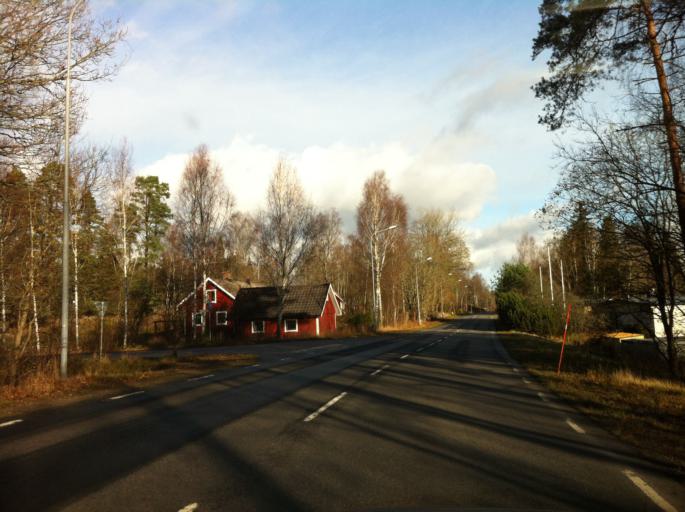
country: SE
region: Kronoberg
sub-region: Almhults Kommun
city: AElmhult
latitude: 56.4730
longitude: 14.0907
